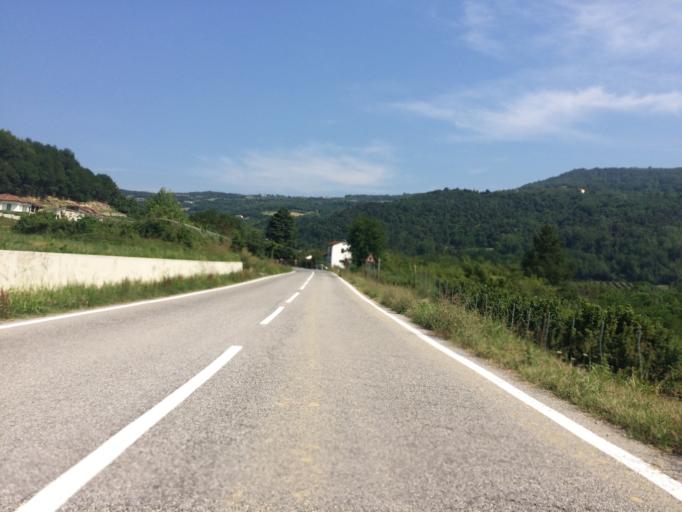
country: IT
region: Piedmont
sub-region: Provincia di Cuneo
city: Torre Bormida
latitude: 44.5602
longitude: 8.1516
